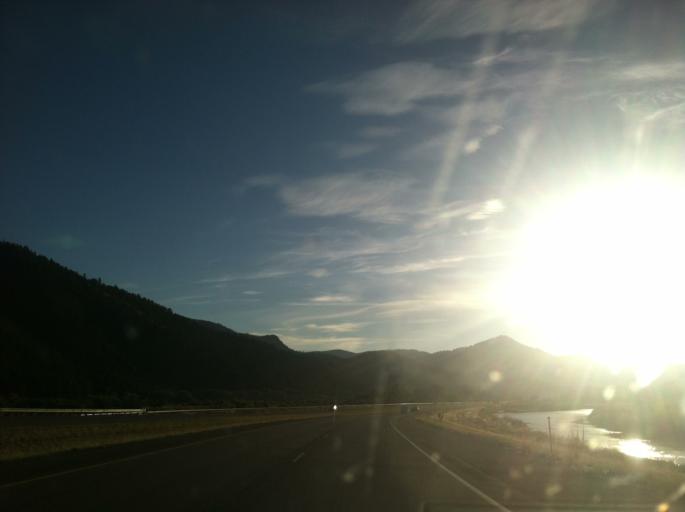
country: US
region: Montana
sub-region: Missoula County
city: Clinton
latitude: 46.6995
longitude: -113.3912
